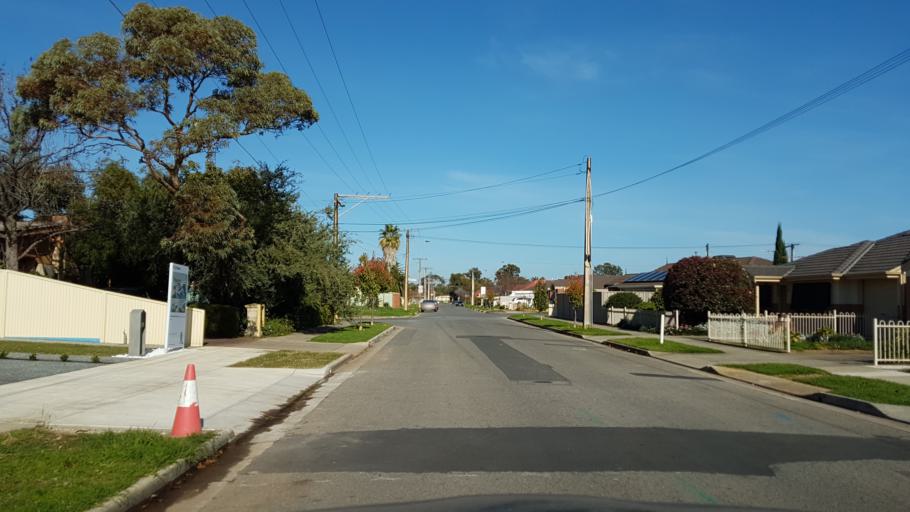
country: AU
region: South Australia
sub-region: Charles Sturt
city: Seaton
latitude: -34.8991
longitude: 138.5177
